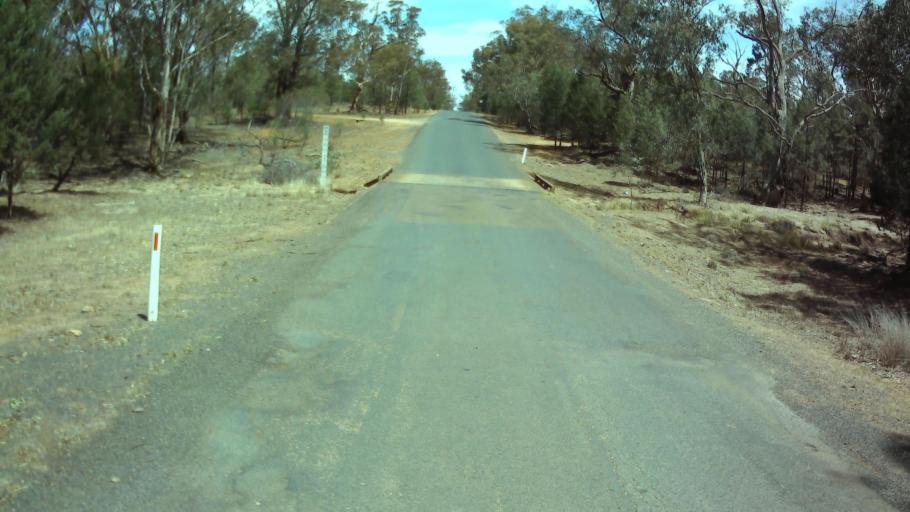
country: AU
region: New South Wales
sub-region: Weddin
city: Grenfell
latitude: -33.8483
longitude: 147.7436
